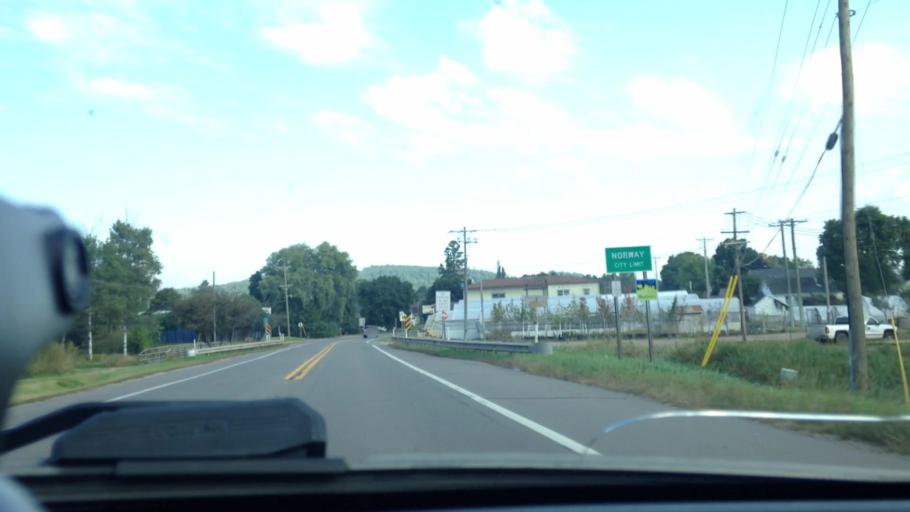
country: US
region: Michigan
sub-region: Dickinson County
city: Norway
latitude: 45.7796
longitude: -87.9094
